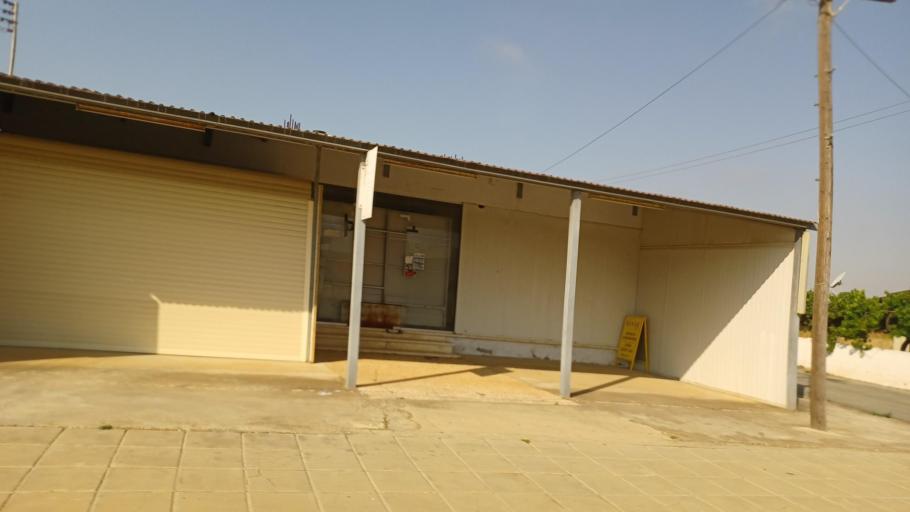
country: CY
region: Ammochostos
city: Avgorou
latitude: 35.0411
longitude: 33.8350
